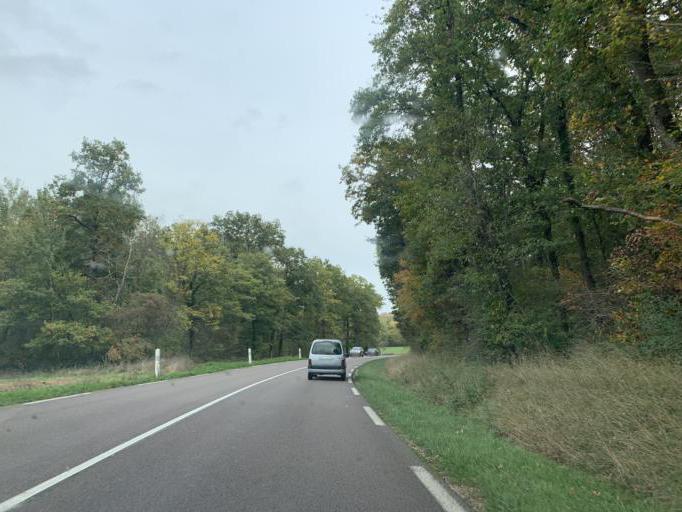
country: FR
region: Bourgogne
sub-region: Departement de l'Yonne
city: Moneteau
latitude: 47.8485
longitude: 3.6228
